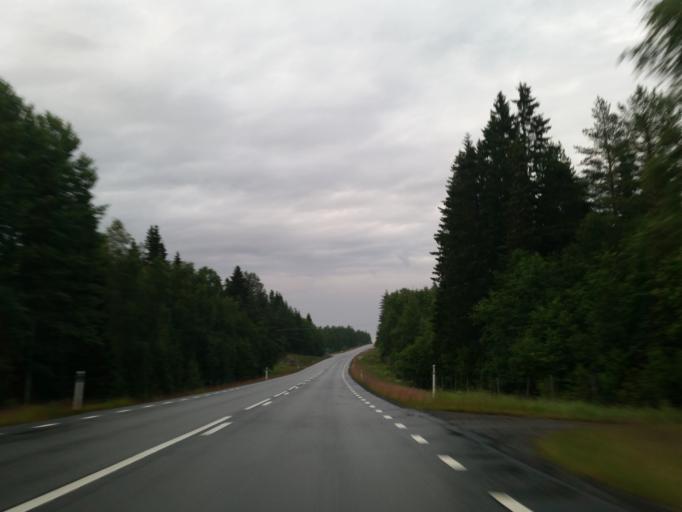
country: SE
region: Vaesterbotten
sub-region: Robertsfors Kommun
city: Robertsfors
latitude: 64.0112
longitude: 20.8140
